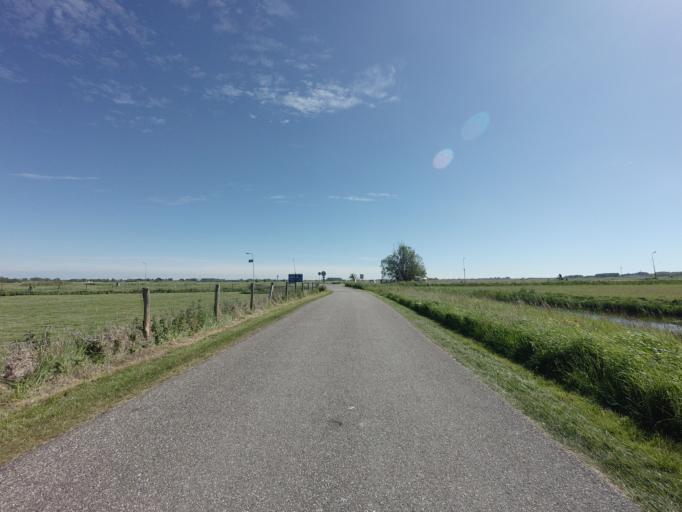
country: NL
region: North Holland
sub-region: Gemeente Uitgeest
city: Uitgeest
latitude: 52.5266
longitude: 4.7335
